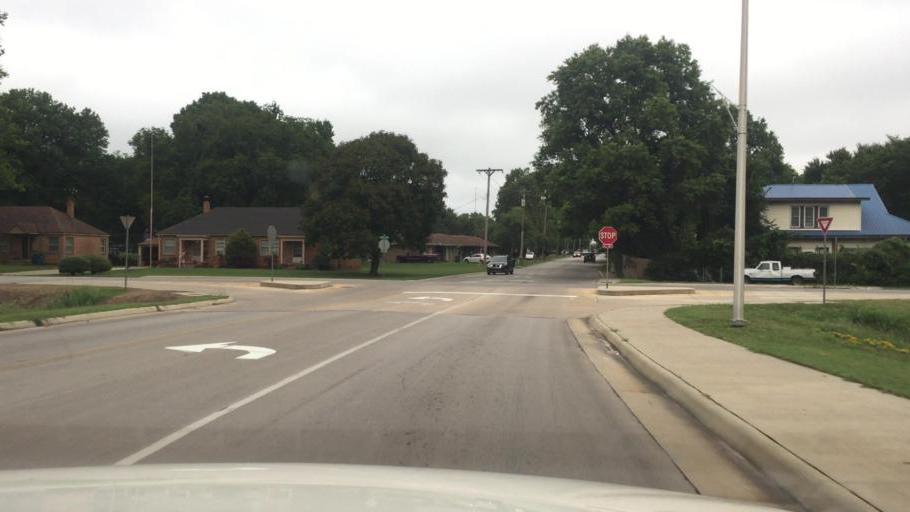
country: US
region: Kansas
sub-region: Montgomery County
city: Coffeyville
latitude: 37.0359
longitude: -95.6469
